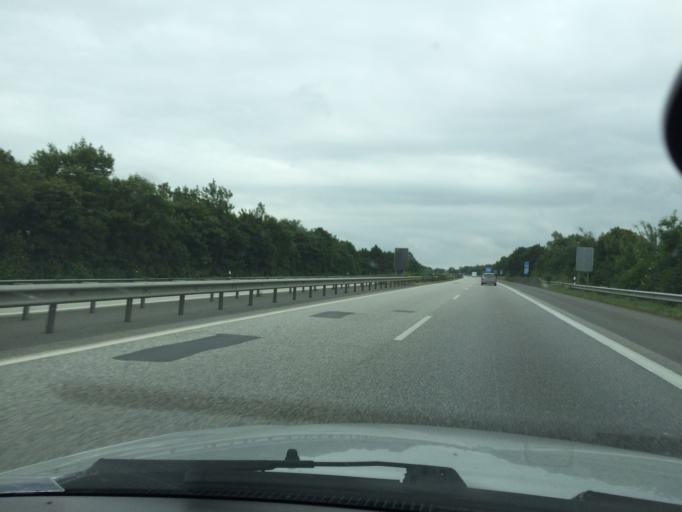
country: DE
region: Schleswig-Holstein
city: Handewitt
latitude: 54.7781
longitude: 9.3425
